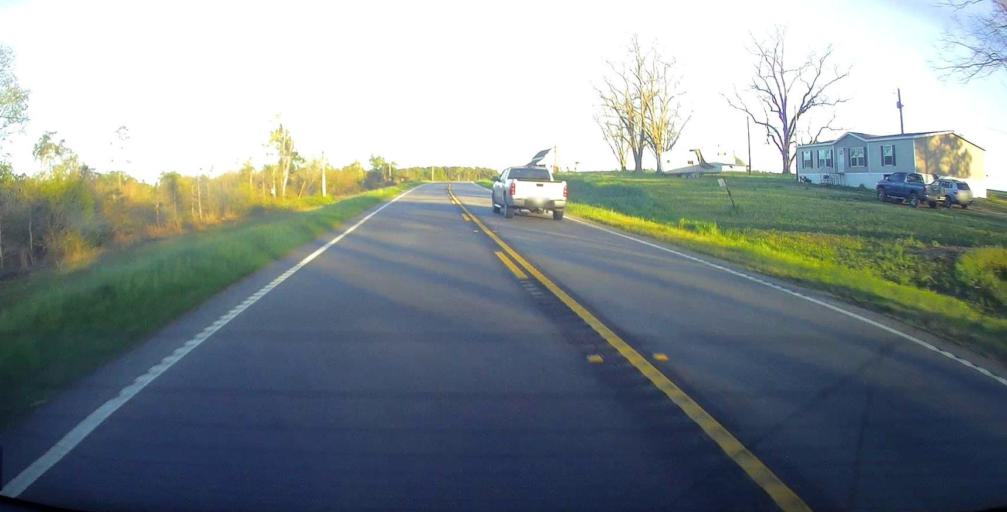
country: US
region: Georgia
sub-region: Crisp County
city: Cordele
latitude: 31.9559
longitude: -83.7292
